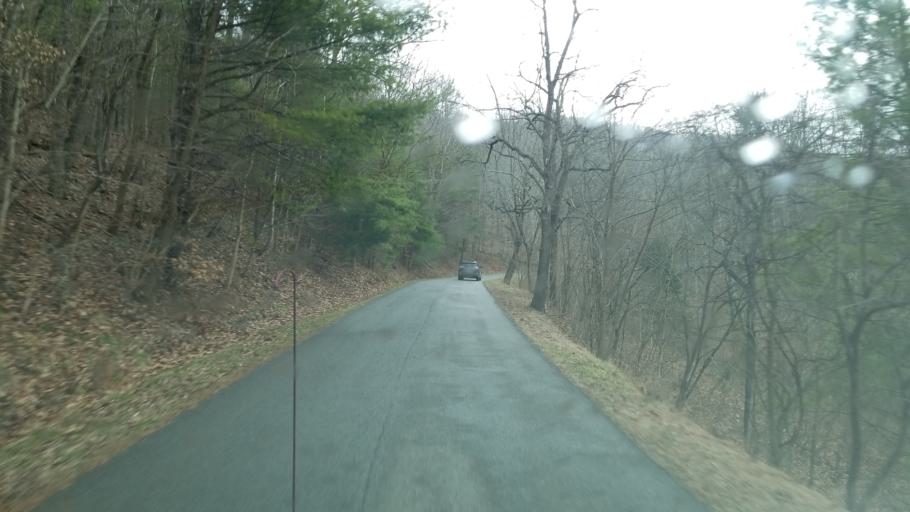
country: US
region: Virginia
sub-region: Giles County
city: Pearisburg
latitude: 37.2201
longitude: -80.7003
